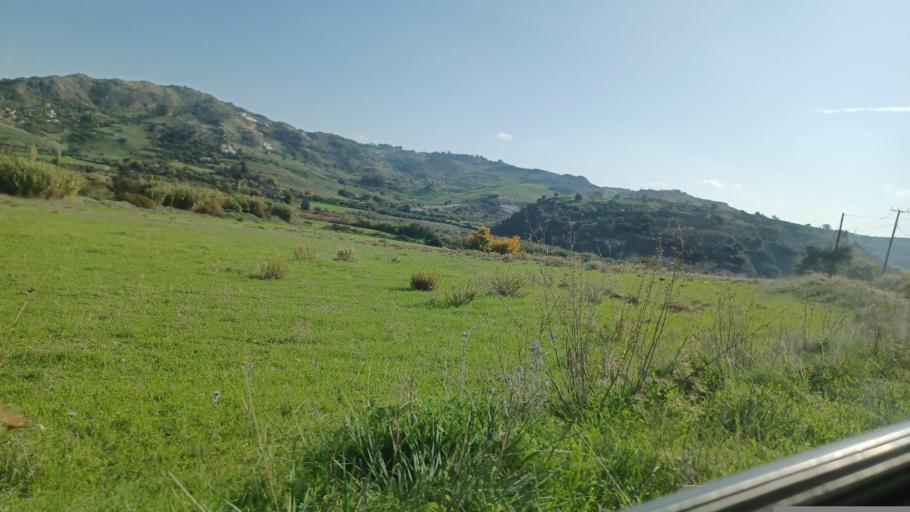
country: CY
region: Pafos
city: Mesogi
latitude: 34.7713
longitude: 32.5747
